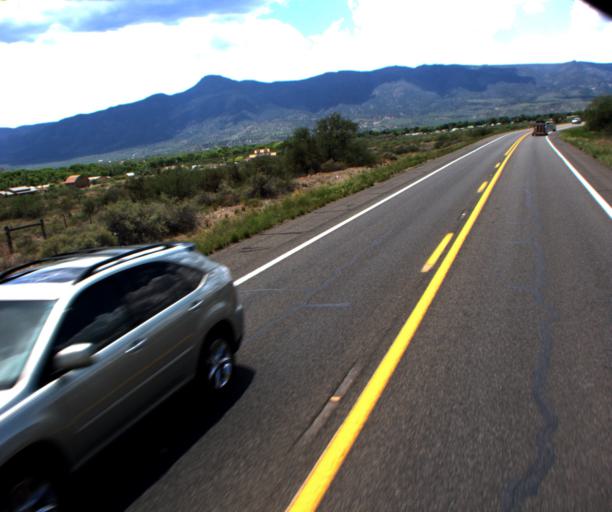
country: US
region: Arizona
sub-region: Yavapai County
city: Camp Verde
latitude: 34.5274
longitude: -111.8011
